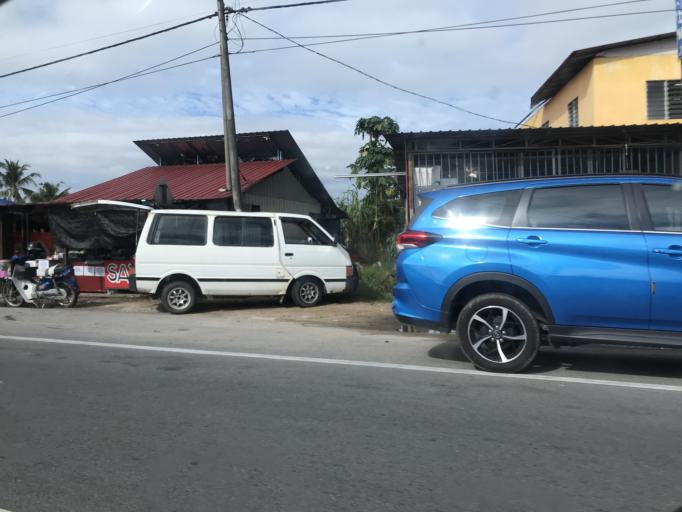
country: MY
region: Kelantan
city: Kota Bharu
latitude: 6.1271
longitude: 102.1804
